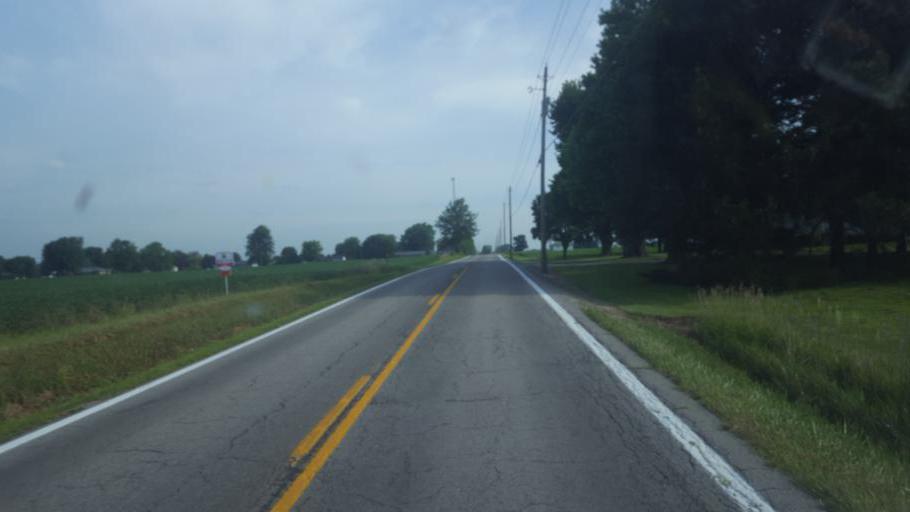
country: US
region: Ohio
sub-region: Marion County
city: Prospect
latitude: 40.5246
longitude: -83.1898
